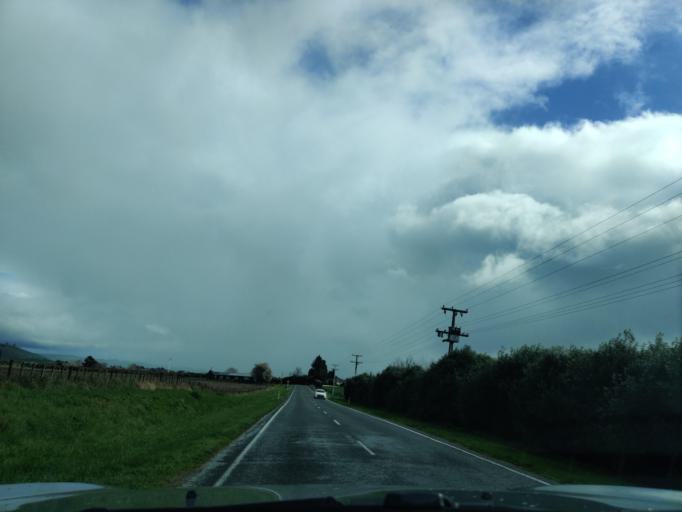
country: NZ
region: Hawke's Bay
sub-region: Hastings District
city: Hastings
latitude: -39.6782
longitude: 176.8296
